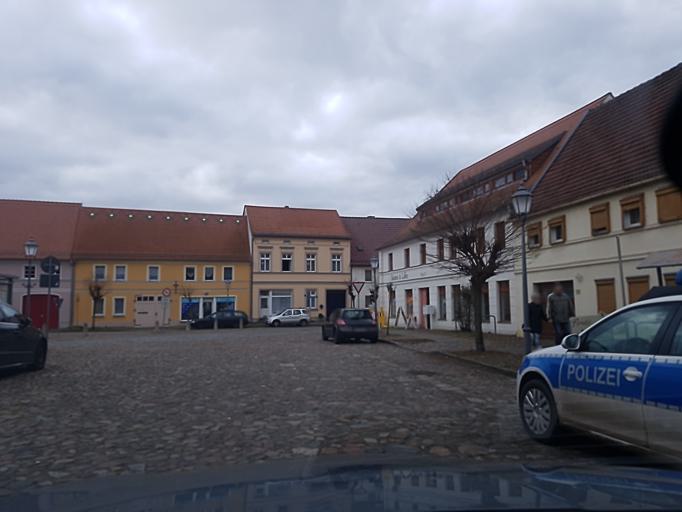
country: DE
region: Brandenburg
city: Falkenberg
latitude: 51.5949
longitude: 13.2999
